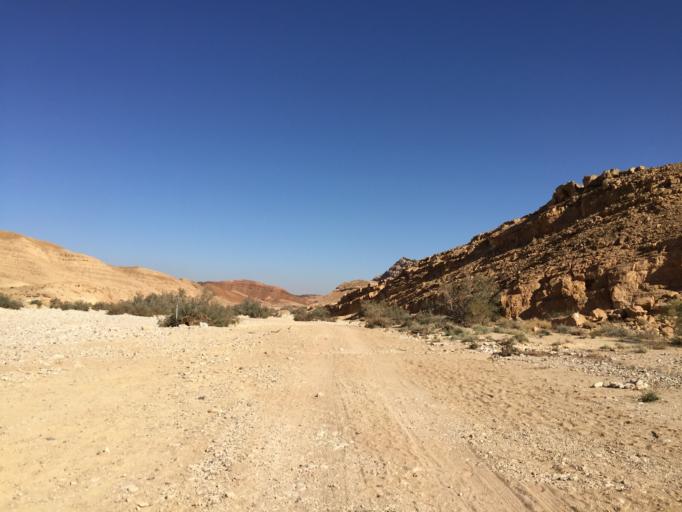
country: IL
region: Southern District
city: Mitzpe Ramon
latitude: 30.6011
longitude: 34.9485
